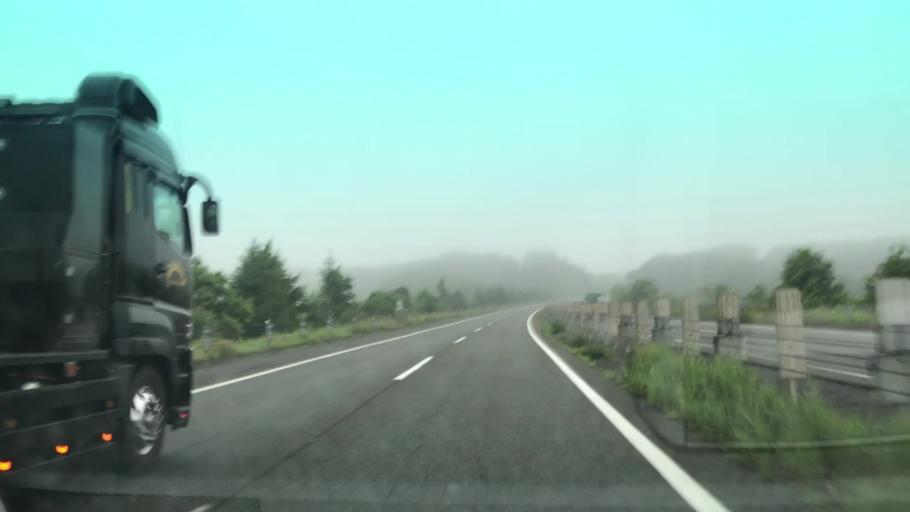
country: JP
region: Hokkaido
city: Tomakomai
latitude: 42.6566
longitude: 141.5732
